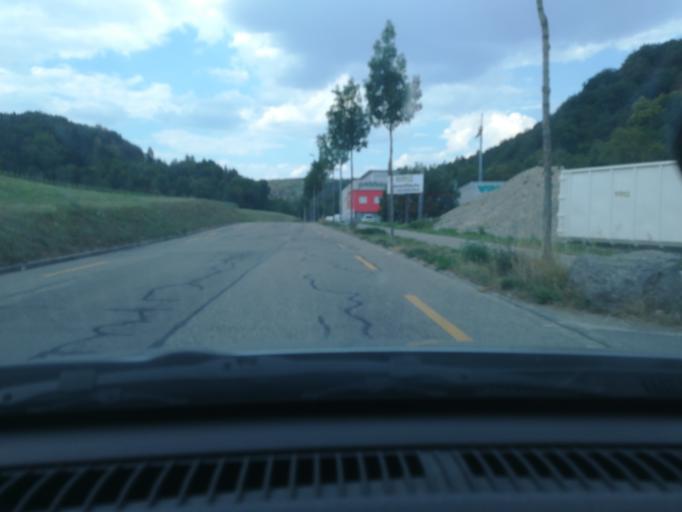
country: CH
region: Schaffhausen
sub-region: Bezirk Schaffhausen
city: Schaffhausen
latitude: 47.7177
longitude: 8.6318
